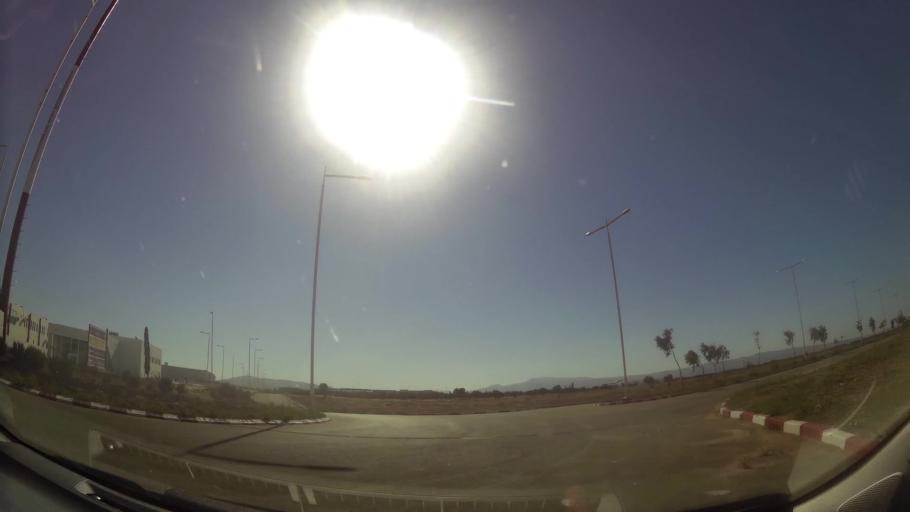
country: MA
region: Oriental
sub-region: Oujda-Angad
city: Oujda
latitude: 34.7704
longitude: -1.9382
